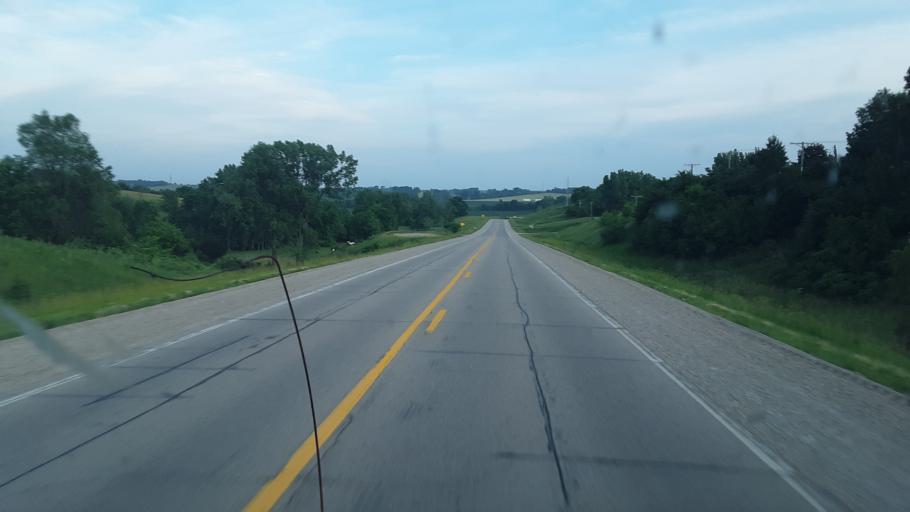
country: US
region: Iowa
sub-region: Benton County
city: Belle Plaine
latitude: 41.7507
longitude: -92.2782
